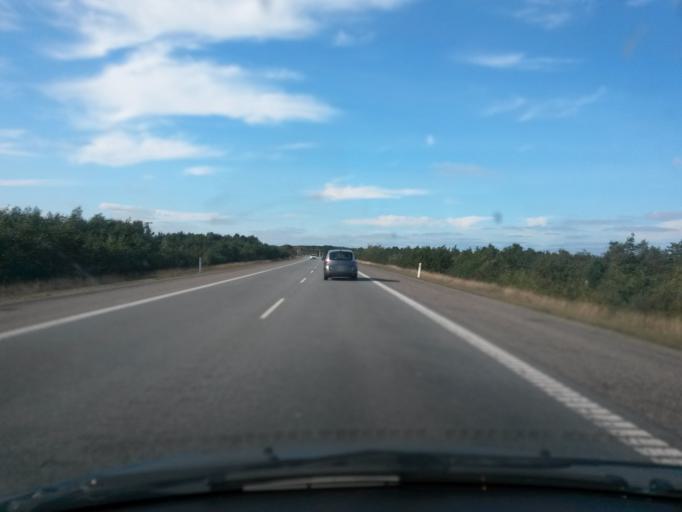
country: DK
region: Central Jutland
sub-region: Herning Kommune
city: Herning
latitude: 56.1750
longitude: 8.9876
